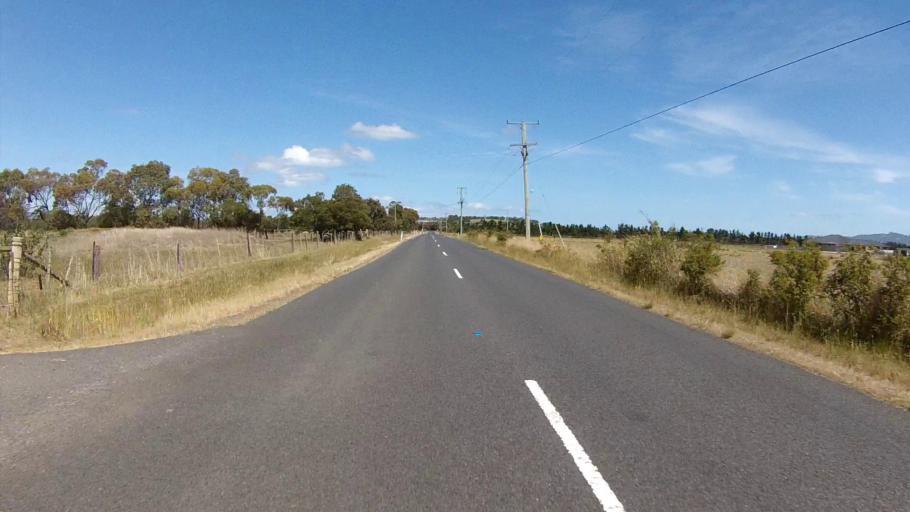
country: AU
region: Tasmania
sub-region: Sorell
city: Sorell
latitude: -42.7745
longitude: 147.5194
